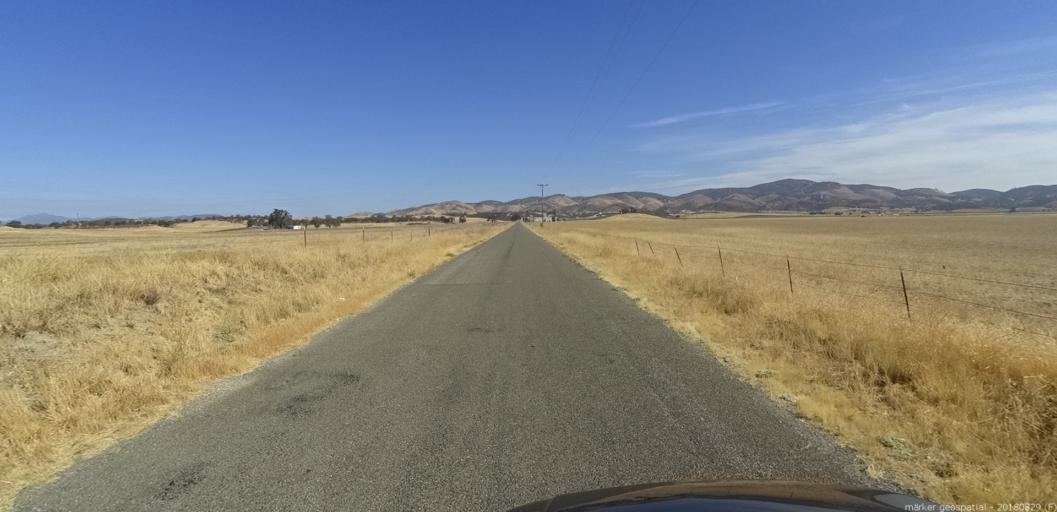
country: US
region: California
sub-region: Monterey County
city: King City
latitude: 35.9595
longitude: -121.1177
